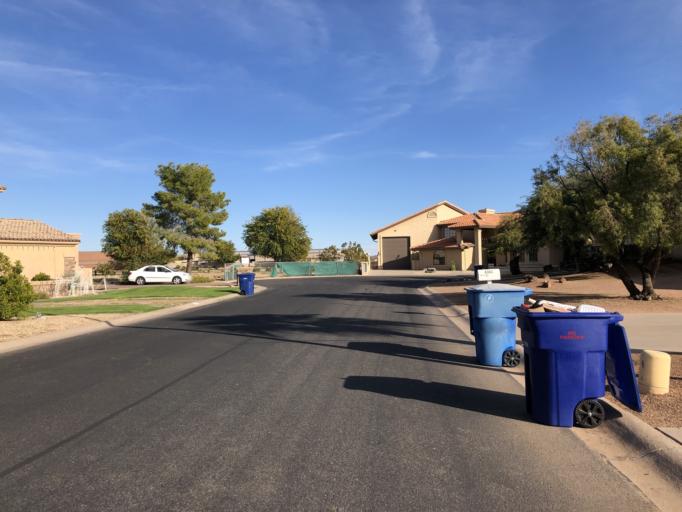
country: US
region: Arizona
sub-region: Maricopa County
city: Chandler
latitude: 33.3021
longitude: -111.9174
